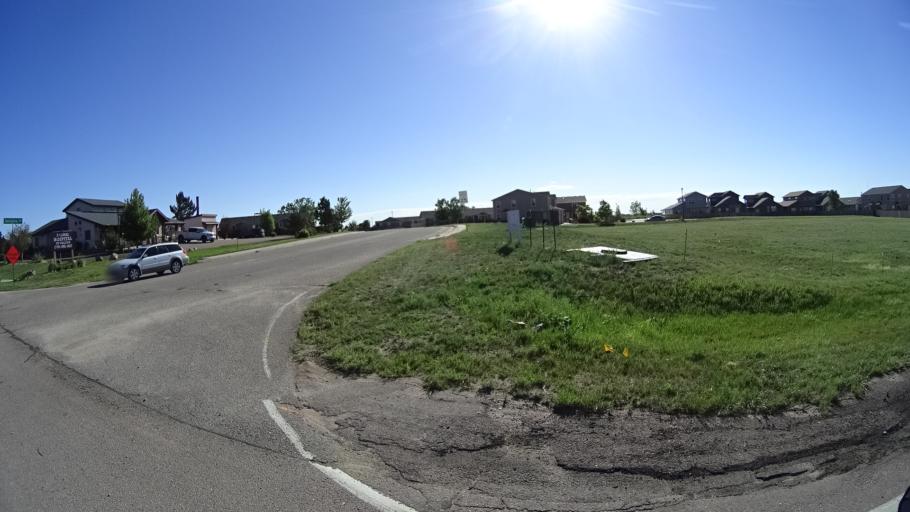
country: US
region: Colorado
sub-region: El Paso County
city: Cimarron Hills
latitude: 38.9299
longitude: -104.6081
